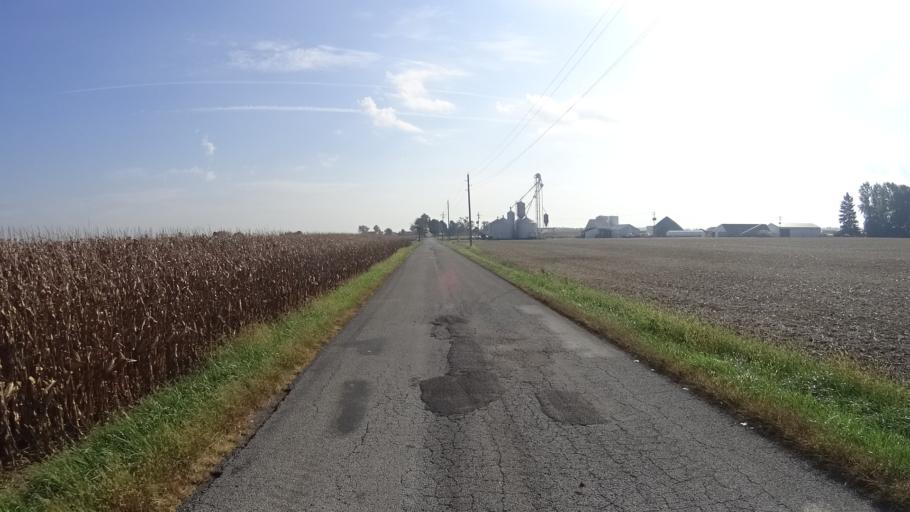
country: US
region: Indiana
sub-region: Madison County
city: Lapel
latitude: 40.0457
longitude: -85.8267
